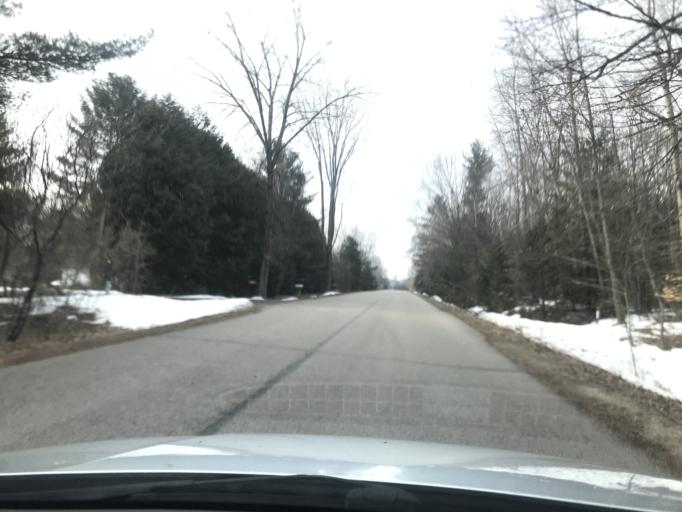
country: US
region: Wisconsin
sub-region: Oconto County
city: Oconto Falls
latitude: 44.8543
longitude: -88.1471
